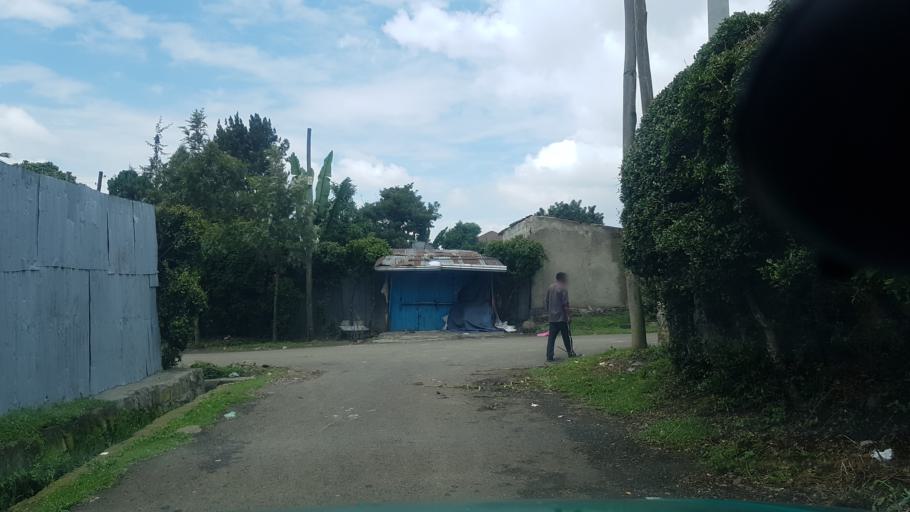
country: ET
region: Adis Abeba
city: Addis Ababa
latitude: 9.0176
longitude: 38.7792
